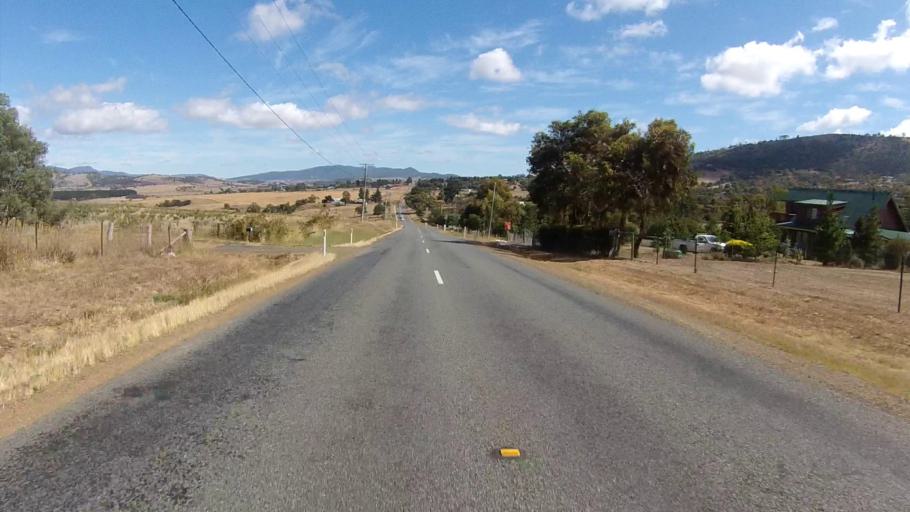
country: AU
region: Tasmania
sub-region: Glenorchy
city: Austins Ferry
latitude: -42.7254
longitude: 147.2842
